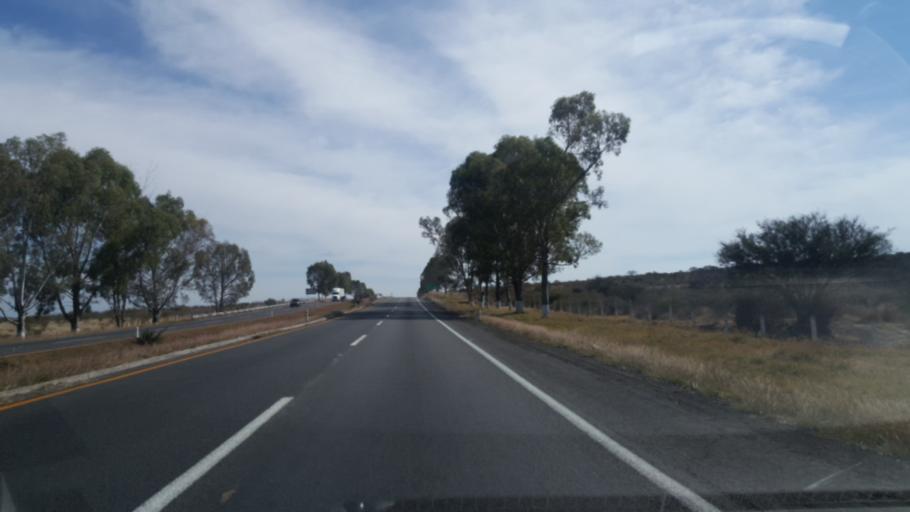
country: MX
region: Jalisco
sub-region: Lagos de Moreno
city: Cristeros [Fraccionamiento]
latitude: 21.2588
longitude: -101.9552
